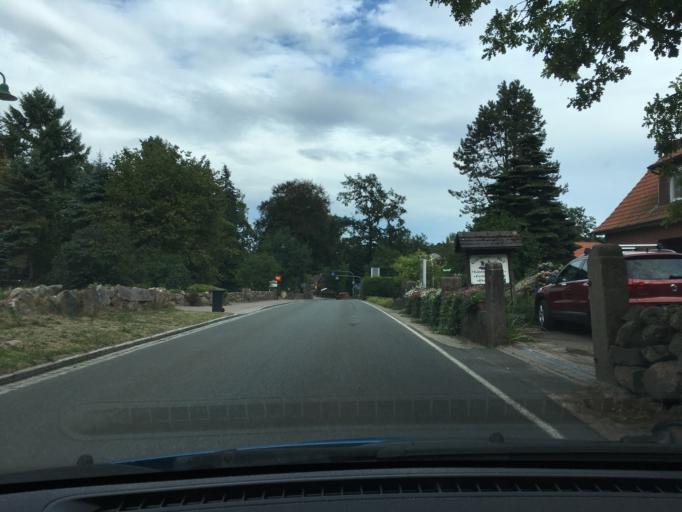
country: DE
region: Lower Saxony
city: Undeloh
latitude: 53.1972
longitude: 9.9736
